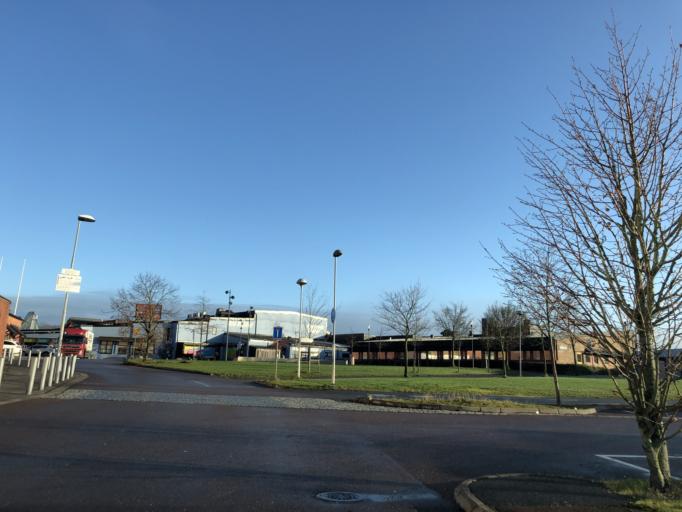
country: SE
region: Vaestra Goetaland
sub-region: Goteborg
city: Hammarkullen
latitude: 57.7948
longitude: 12.0503
